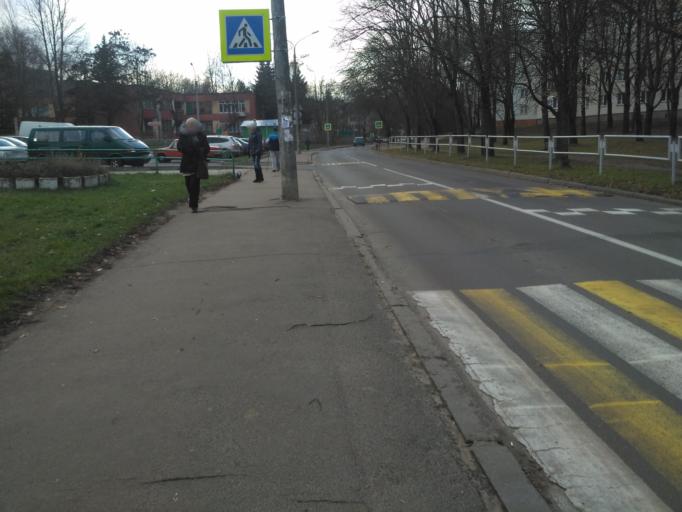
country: BY
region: Minsk
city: Novoye Medvezhino
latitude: 53.9212
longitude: 27.4923
